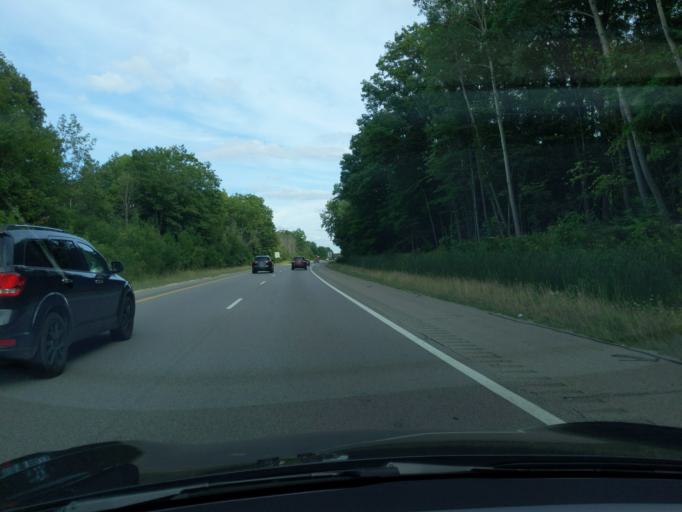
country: US
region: Michigan
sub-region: Ottawa County
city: Coopersville
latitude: 43.0730
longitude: -86.0419
